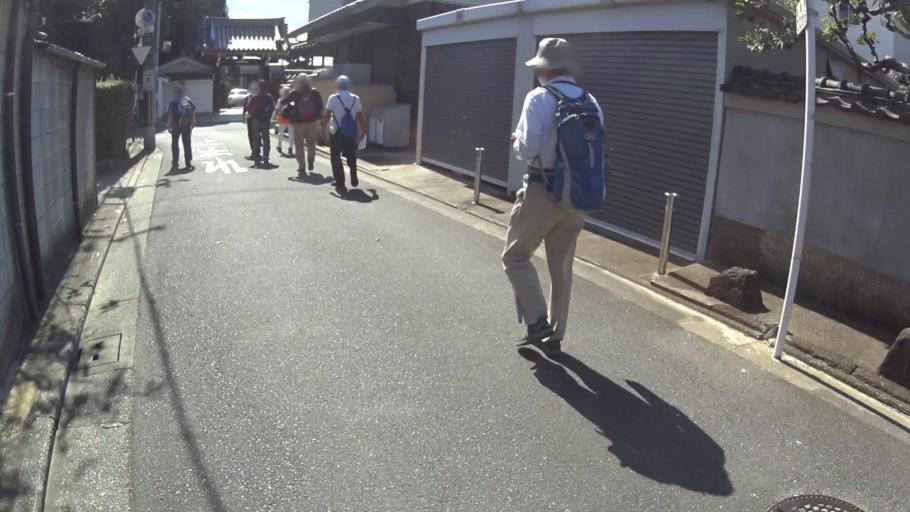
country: JP
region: Osaka
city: Izumiotsu
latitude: 34.4861
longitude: 135.4006
